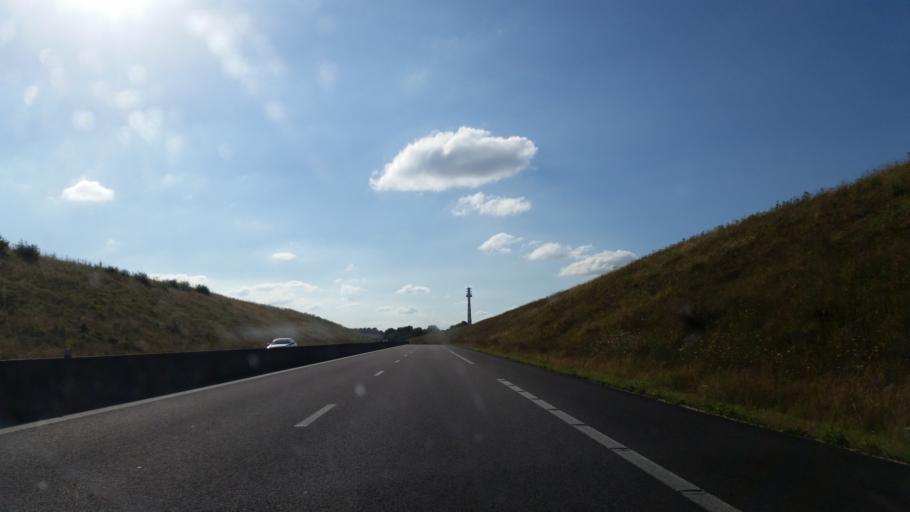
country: FR
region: Haute-Normandie
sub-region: Departement de la Seine-Maritime
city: Gaillefontaine
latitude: 49.7406
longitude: 1.6024
